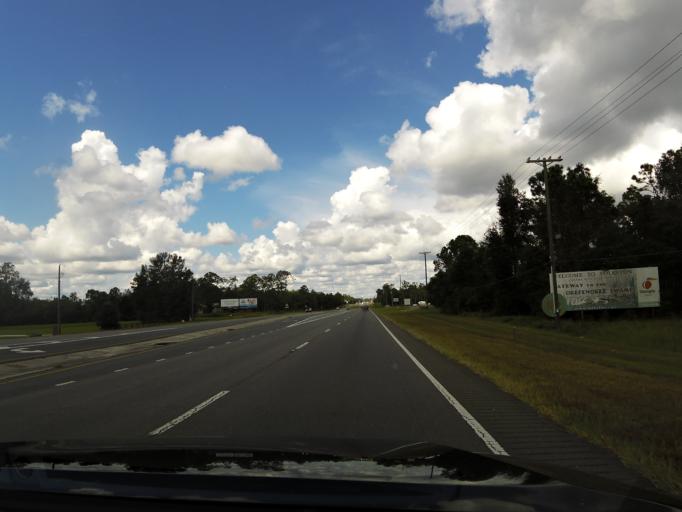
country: US
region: Georgia
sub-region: Charlton County
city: Folkston
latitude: 30.8125
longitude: -81.9982
